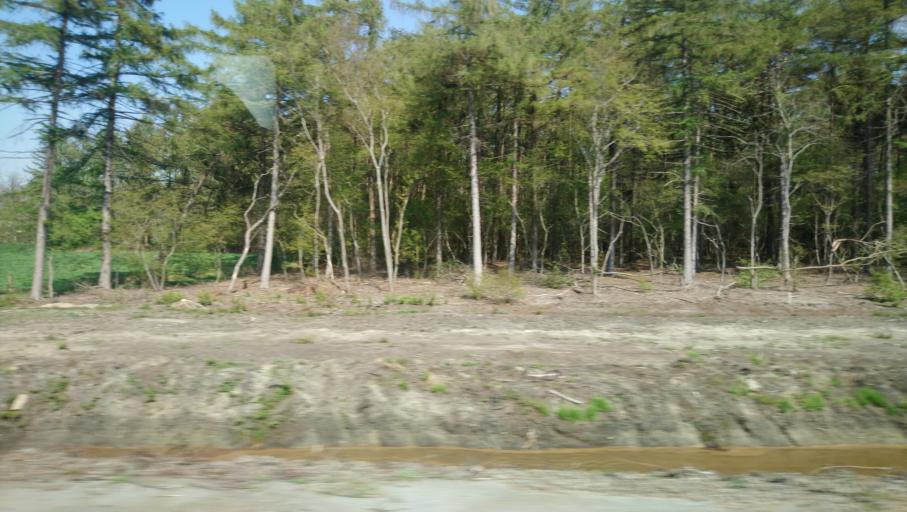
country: BE
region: Flanders
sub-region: Provincie West-Vlaanderen
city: Beernem
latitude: 51.1173
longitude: 3.3596
